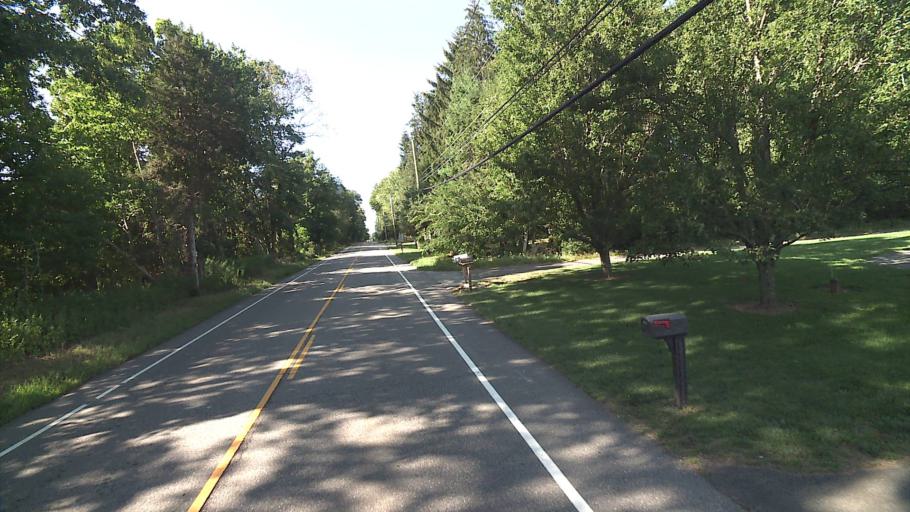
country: US
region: Connecticut
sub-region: New Haven County
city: Cheshire Village
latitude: 41.5162
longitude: -72.8715
